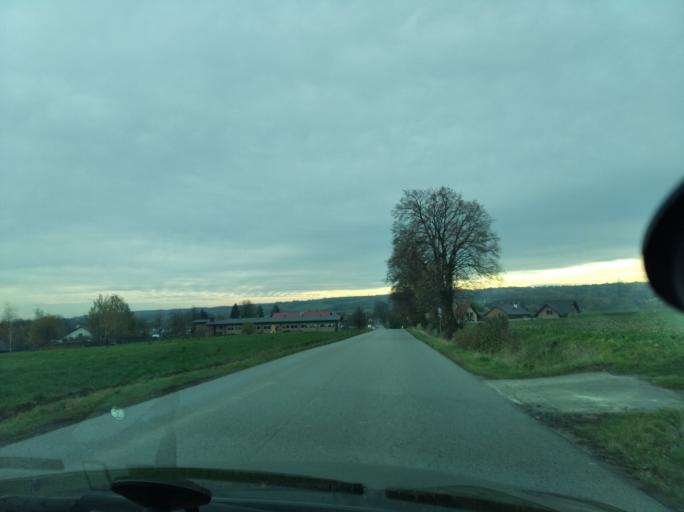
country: PL
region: Subcarpathian Voivodeship
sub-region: Powiat lancucki
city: Wysoka
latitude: 50.0214
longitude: 22.2601
